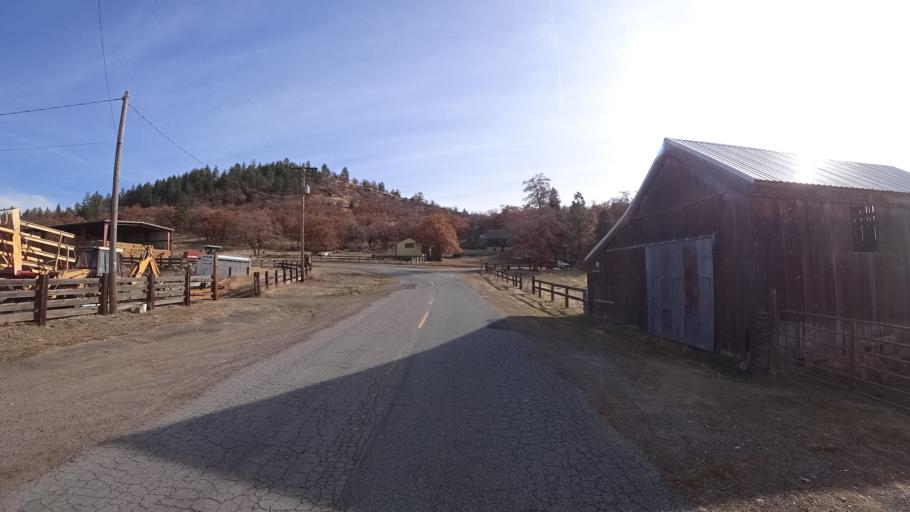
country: US
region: California
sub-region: Siskiyou County
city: Weed
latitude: 41.4672
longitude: -122.4140
